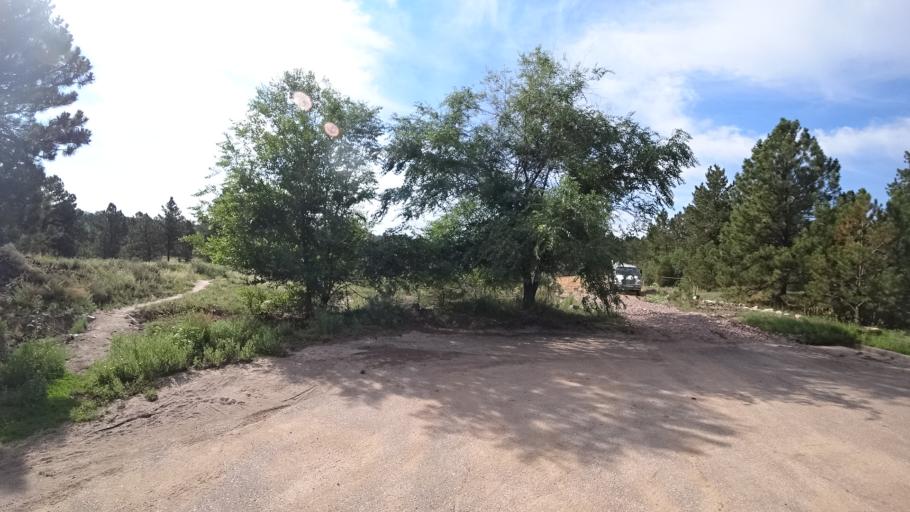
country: US
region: Colorado
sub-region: El Paso County
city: Air Force Academy
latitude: 38.9405
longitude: -104.8231
